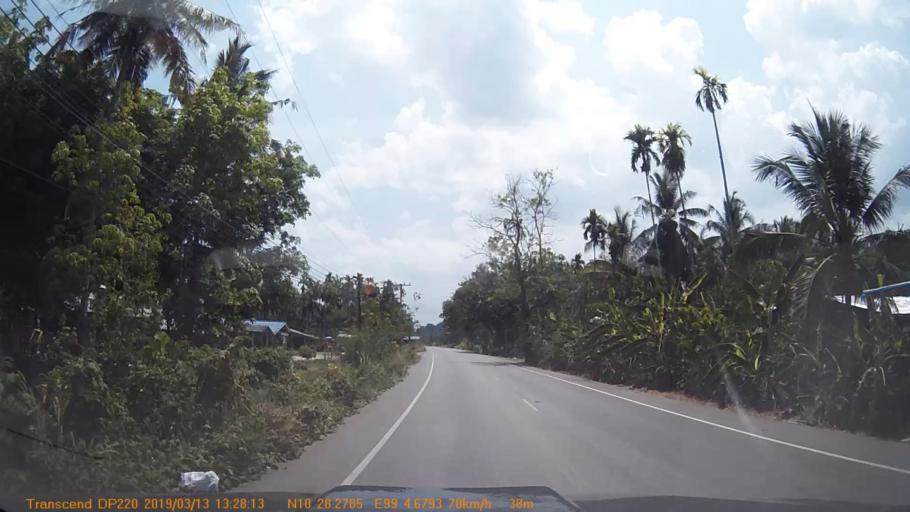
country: TH
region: Chumphon
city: Chumphon
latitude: 10.4759
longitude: 99.0779
